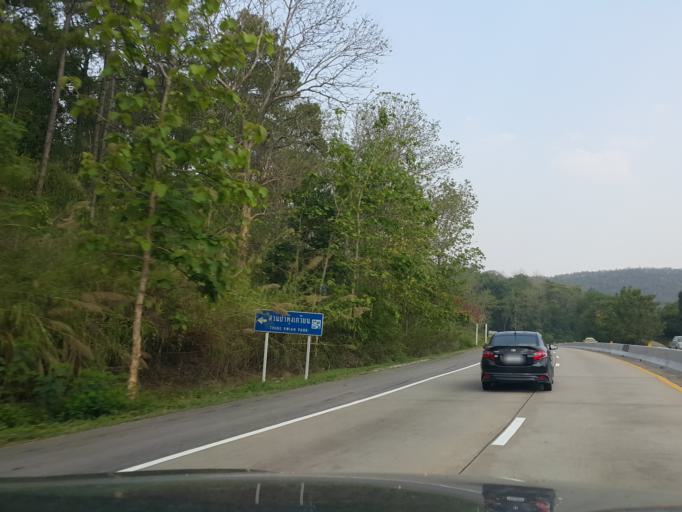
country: TH
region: Lampang
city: Hang Chat
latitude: 18.3366
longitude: 99.2477
